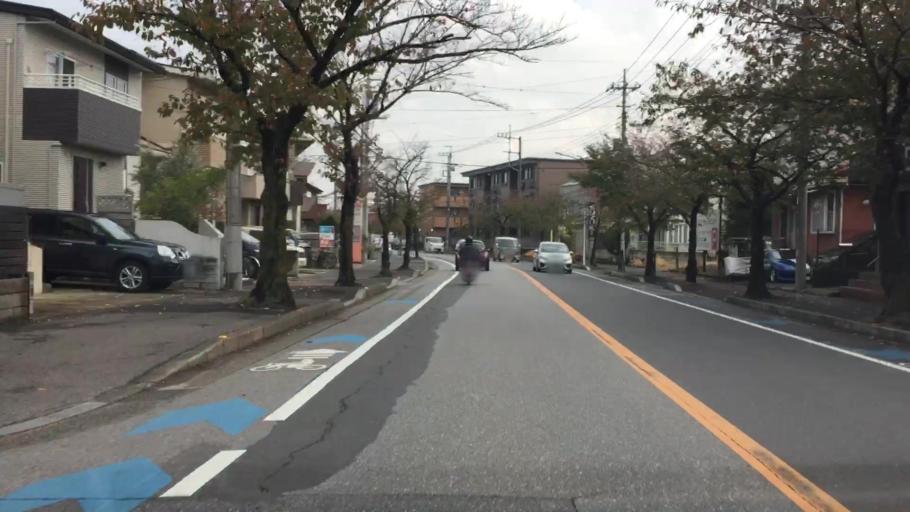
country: JP
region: Chiba
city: Kashiwa
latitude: 35.8433
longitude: 139.9755
